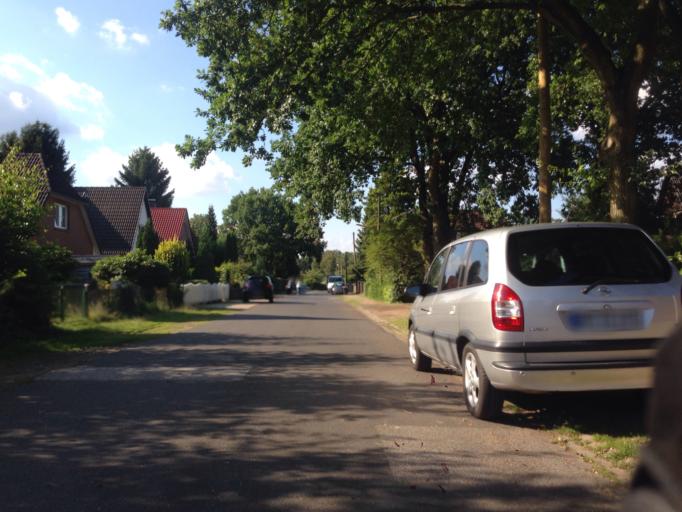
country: DE
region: Hamburg
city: Farmsen-Berne
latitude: 53.5891
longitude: 10.1198
